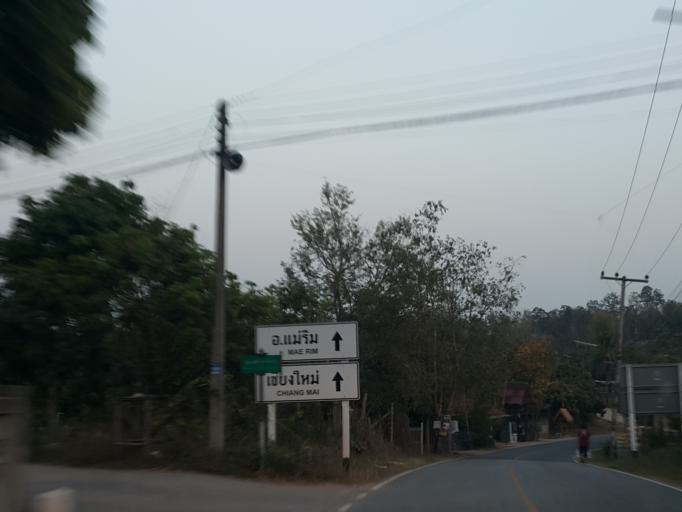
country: TH
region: Chiang Mai
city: Mae Taeng
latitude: 18.9867
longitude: 98.9060
